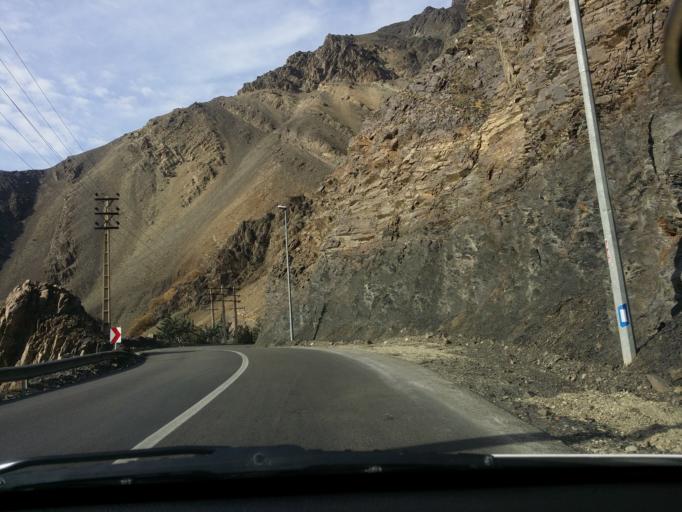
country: IR
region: Alborz
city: Karaj
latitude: 36.0024
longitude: 51.1167
